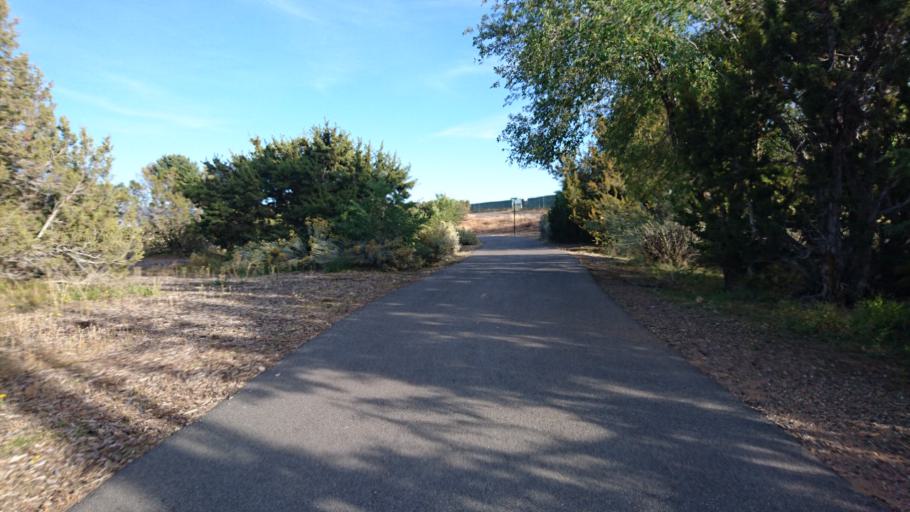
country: US
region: New Mexico
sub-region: Santa Fe County
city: Agua Fria
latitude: 35.6428
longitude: -106.0003
